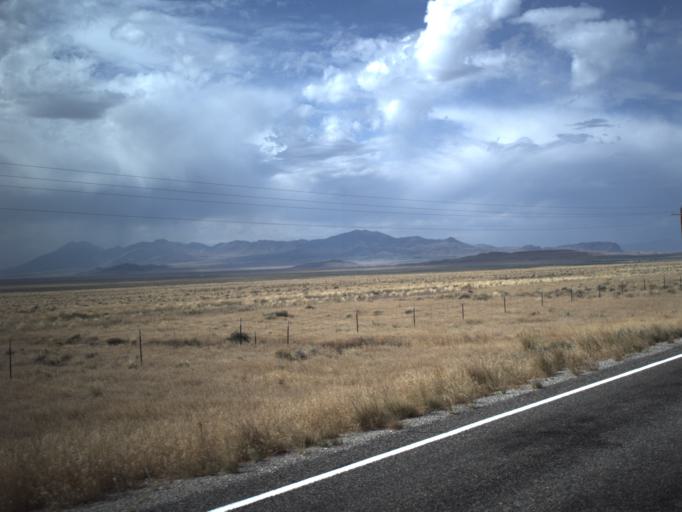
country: US
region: Utah
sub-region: Tooele County
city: Wendover
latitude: 41.4330
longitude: -113.7802
